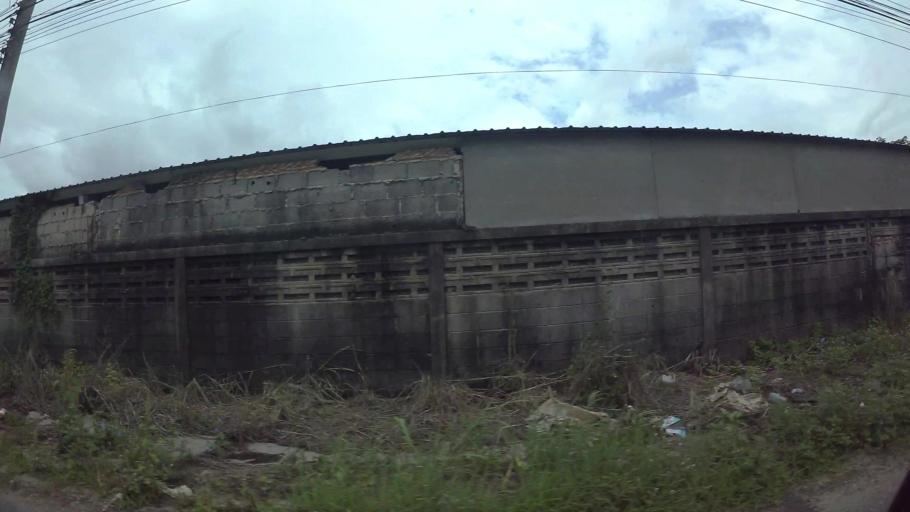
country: TH
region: Chon Buri
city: Si Racha
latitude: 13.1574
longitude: 100.9813
